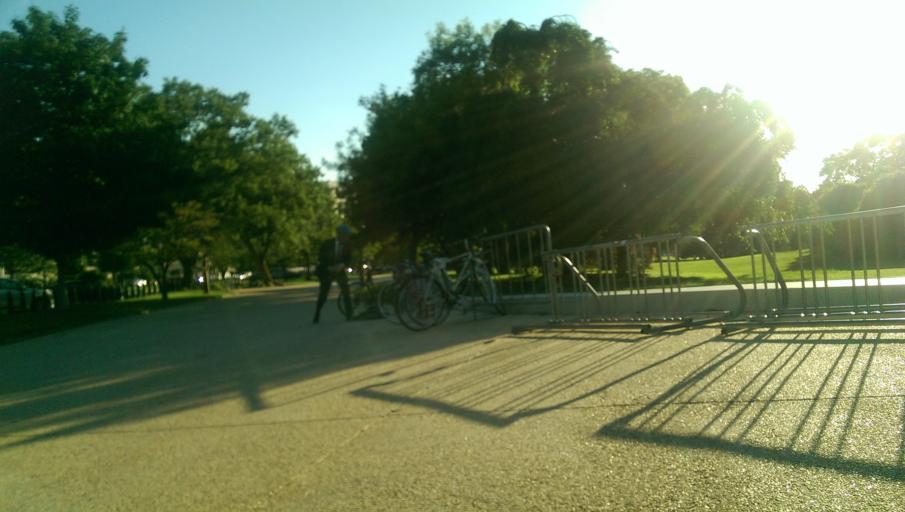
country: US
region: Washington, D.C.
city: Washington, D.C.
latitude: 38.8883
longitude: -77.0086
